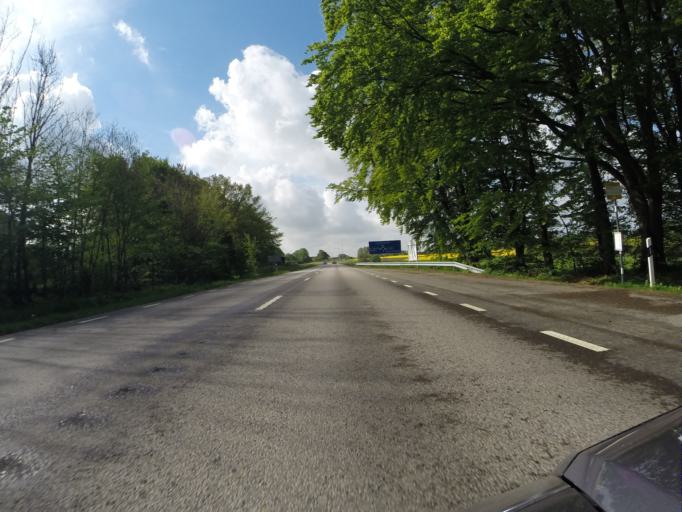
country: SE
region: Skane
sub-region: Bjuvs Kommun
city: Billesholm
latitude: 56.0140
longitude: 12.9577
